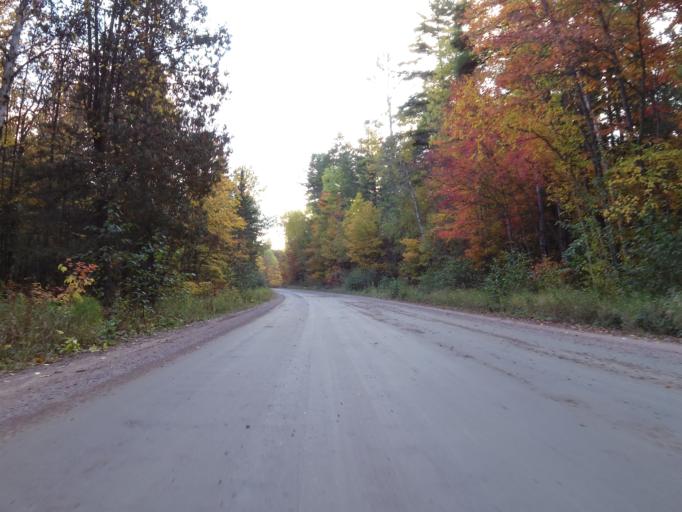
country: CA
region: Ontario
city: Deep River
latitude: 45.8912
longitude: -77.6300
